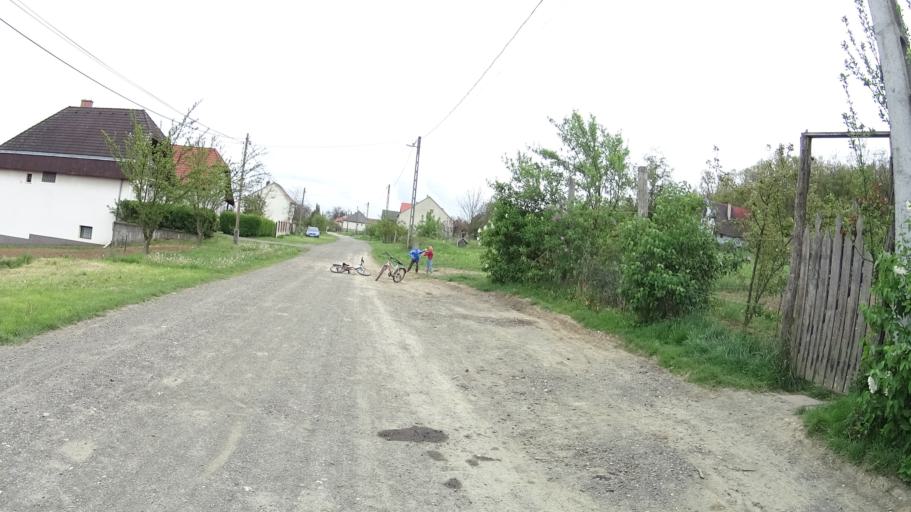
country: HU
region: Pest
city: Acsa
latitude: 47.8150
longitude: 19.3153
